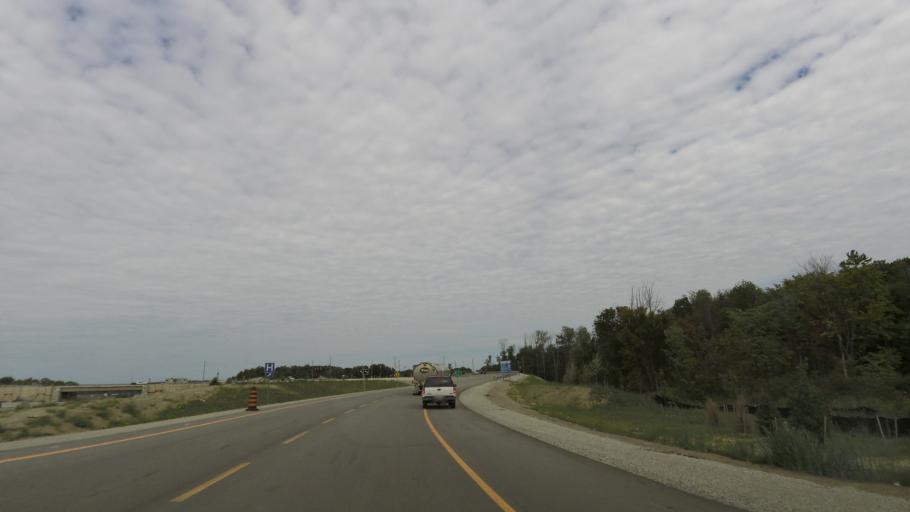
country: CA
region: Ontario
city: Bradford West Gwillimbury
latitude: 44.0271
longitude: -79.5931
